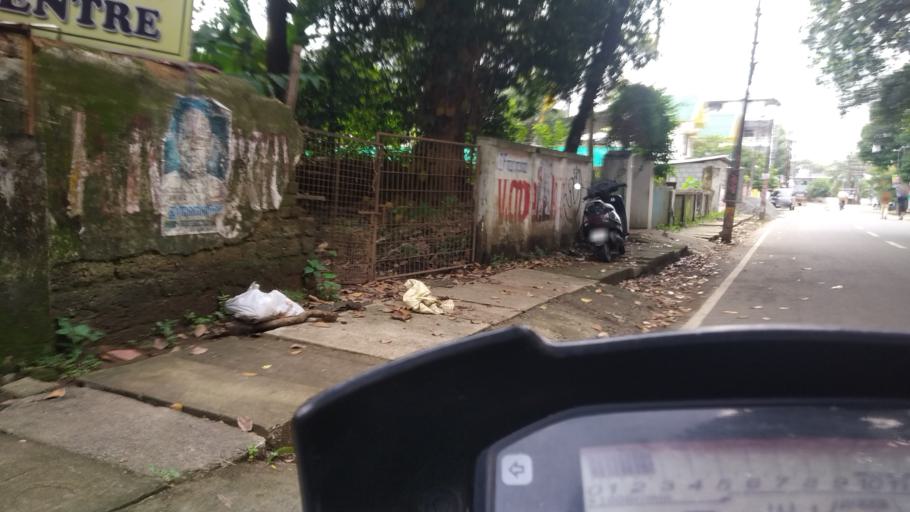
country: IN
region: Kerala
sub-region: Ernakulam
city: Aluva
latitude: 10.1163
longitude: 76.3504
